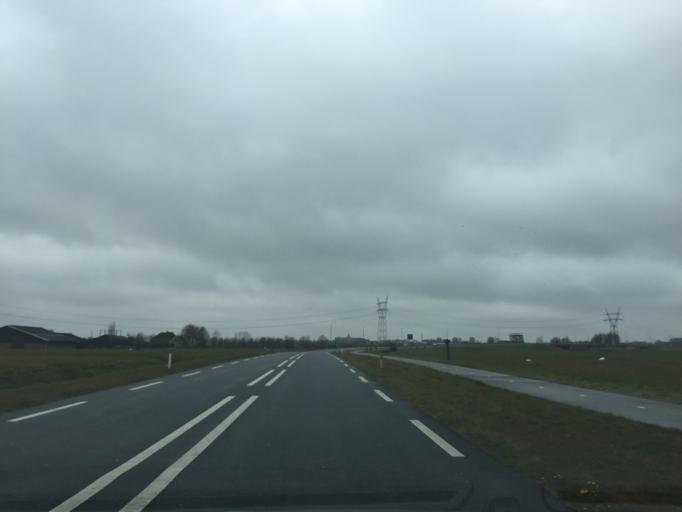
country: NL
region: South Holland
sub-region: Gemeente Leiderdorp
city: Leiderdorp
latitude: 52.1601
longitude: 4.5695
